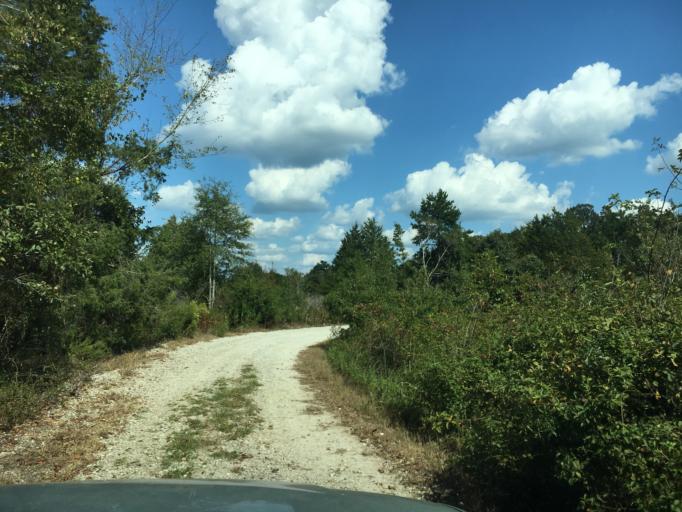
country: US
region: South Carolina
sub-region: Laurens County
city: Laurens
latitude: 34.5823
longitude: -82.1063
